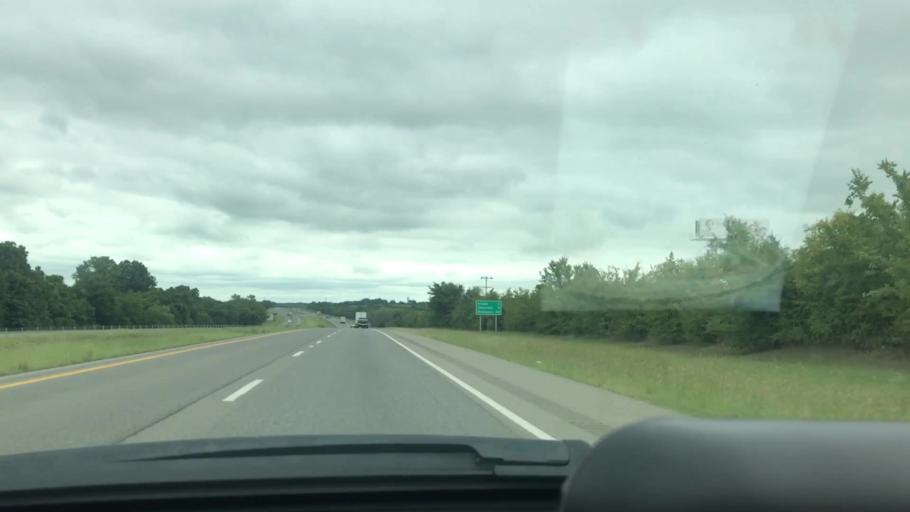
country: US
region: Oklahoma
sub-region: McIntosh County
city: Eufaula
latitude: 35.3735
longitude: -95.5705
